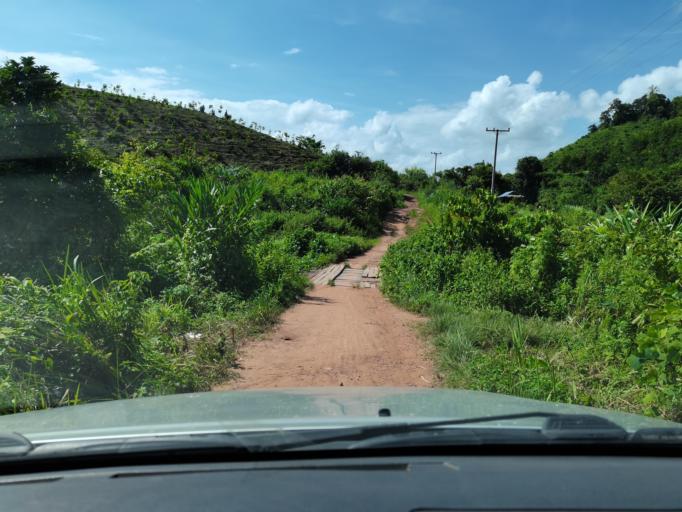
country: LA
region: Loungnamtha
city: Muang Nale
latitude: 20.5622
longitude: 101.0584
